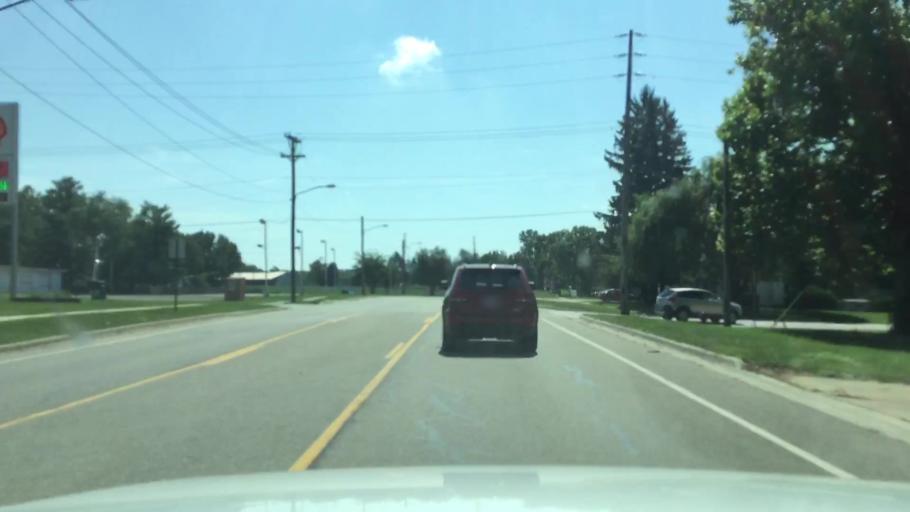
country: US
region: Michigan
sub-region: Lenawee County
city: Clinton
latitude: 42.0666
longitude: -83.9681
